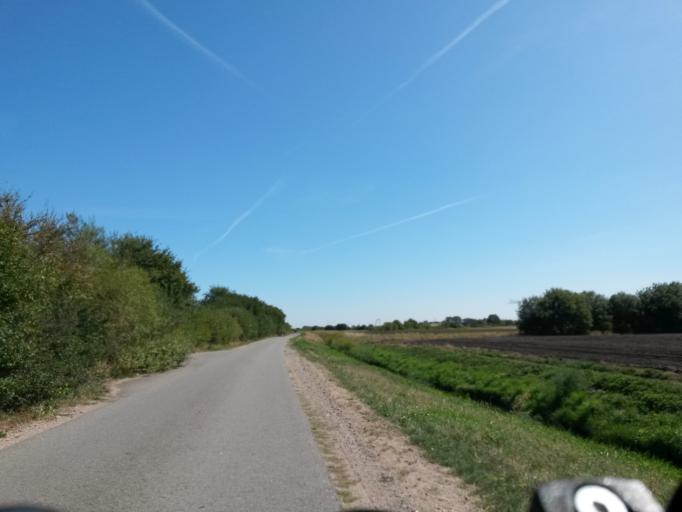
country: DE
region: Saxony-Anhalt
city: Tangermunde
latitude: 52.5755
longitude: 11.9581
